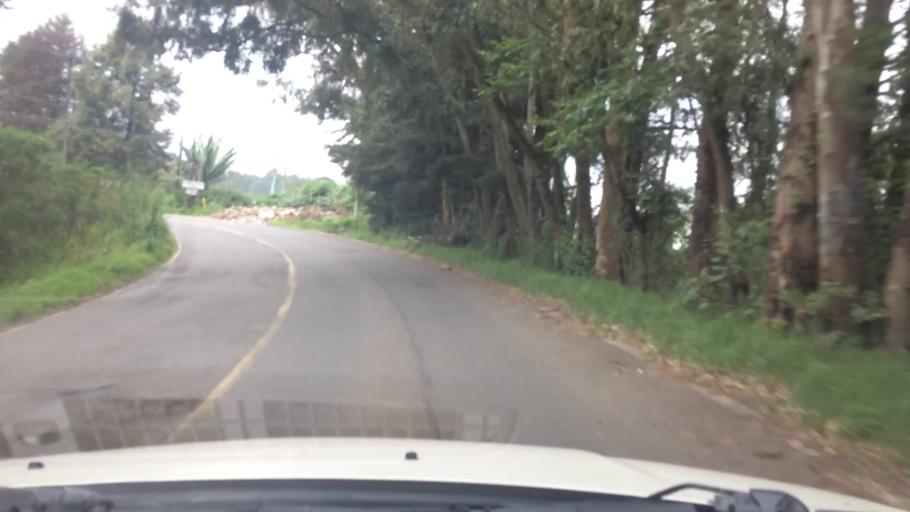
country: MX
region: Mexico
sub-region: Valle de Bravo
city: Cuadrilla de Dolores
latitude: 19.1478
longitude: -100.0662
